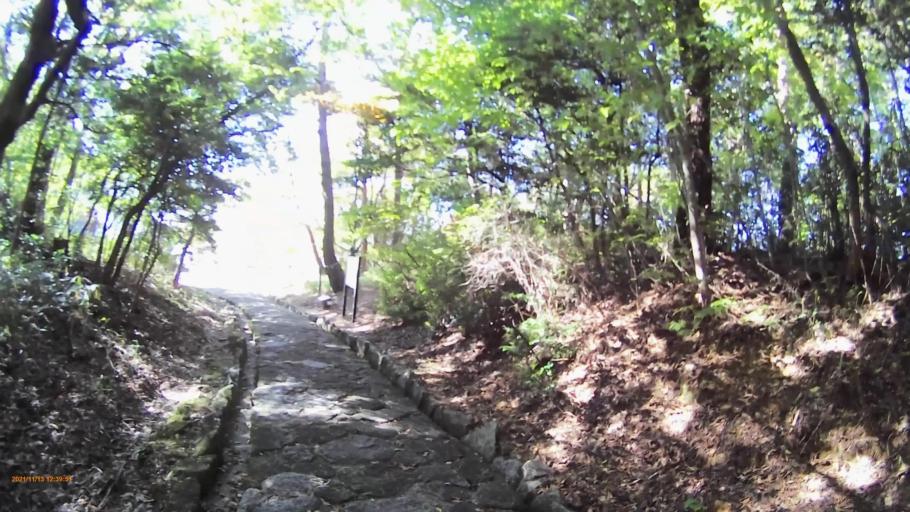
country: JP
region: Gifu
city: Inuyama
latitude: 35.4113
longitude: 136.9516
